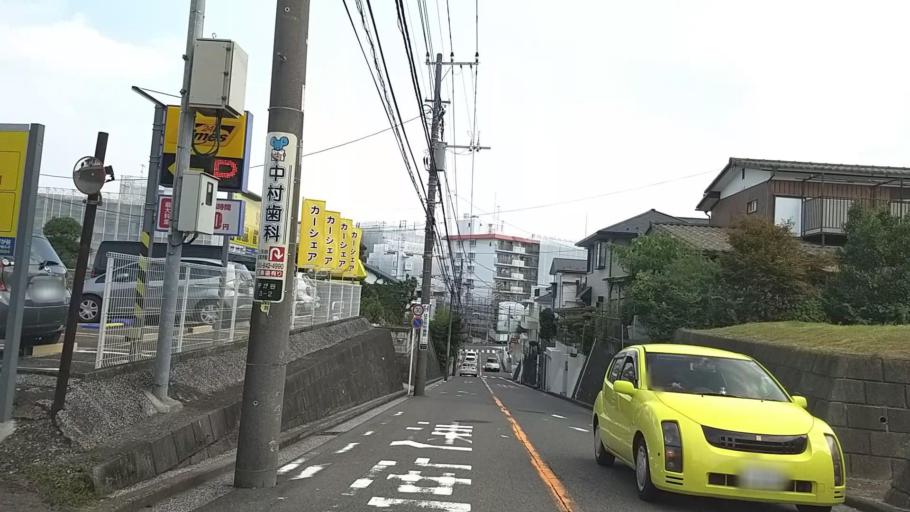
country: JP
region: Kanagawa
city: Yokohama
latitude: 35.4137
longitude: 139.5758
